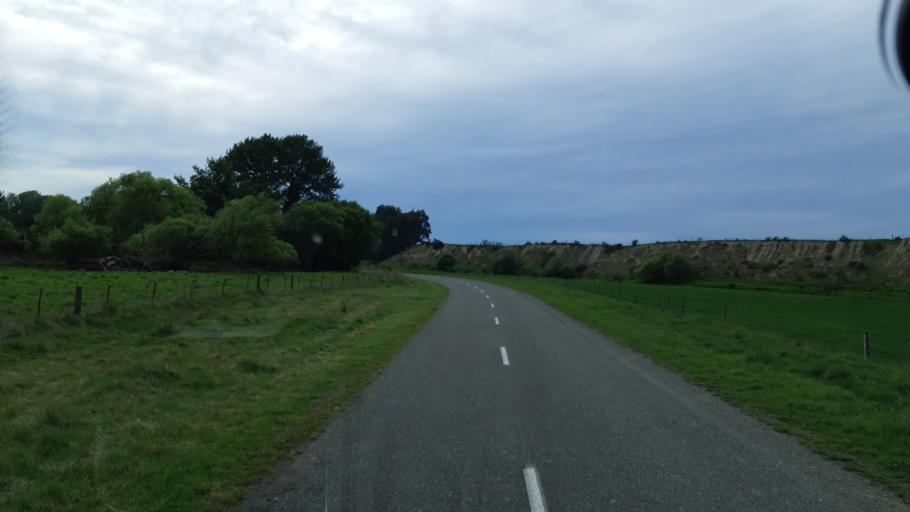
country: NZ
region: Canterbury
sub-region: Timaru District
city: Timaru
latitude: -44.5409
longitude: 171.1400
